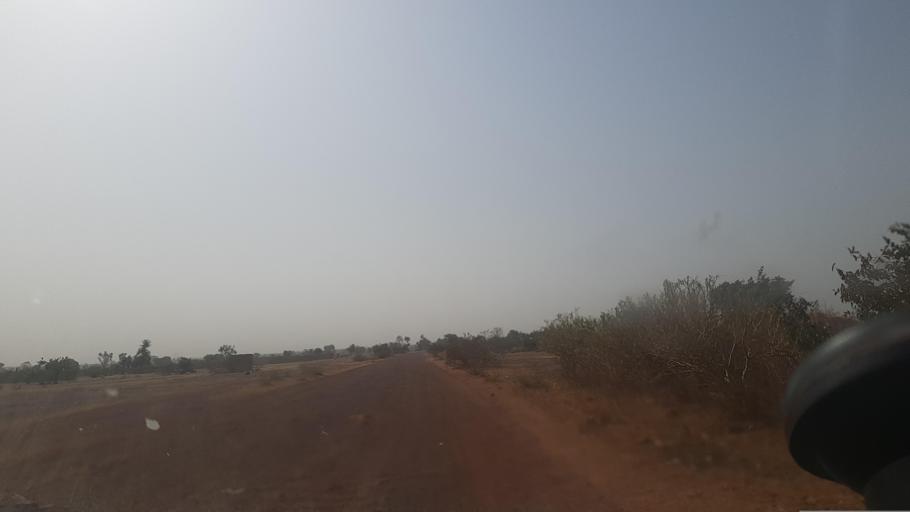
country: ML
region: Segou
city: Baroueli
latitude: 13.1558
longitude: -6.5168
